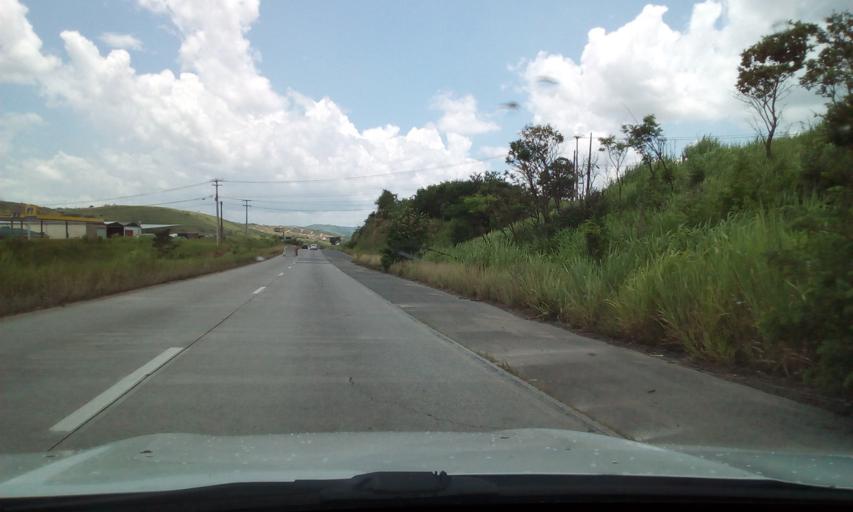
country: BR
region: Pernambuco
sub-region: Vitoria De Santo Antao
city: Vitoria de Santo Antao
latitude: -8.1183
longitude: -35.2628
